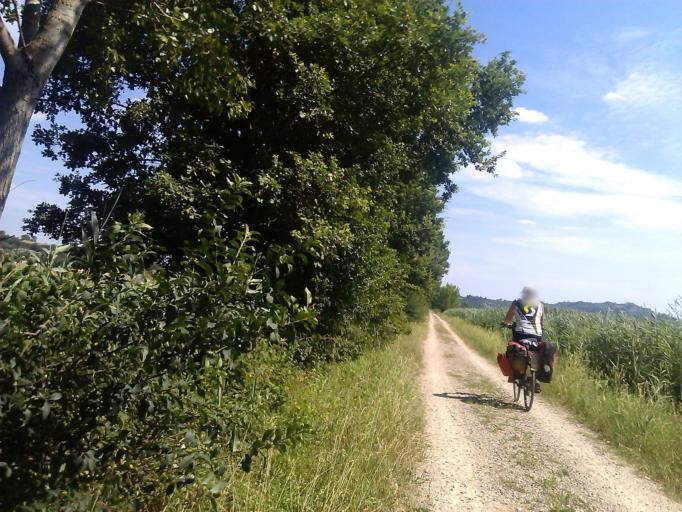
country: IT
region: Tuscany
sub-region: Provincia di Siena
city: Chiusi
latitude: 43.0665
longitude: 11.9298
